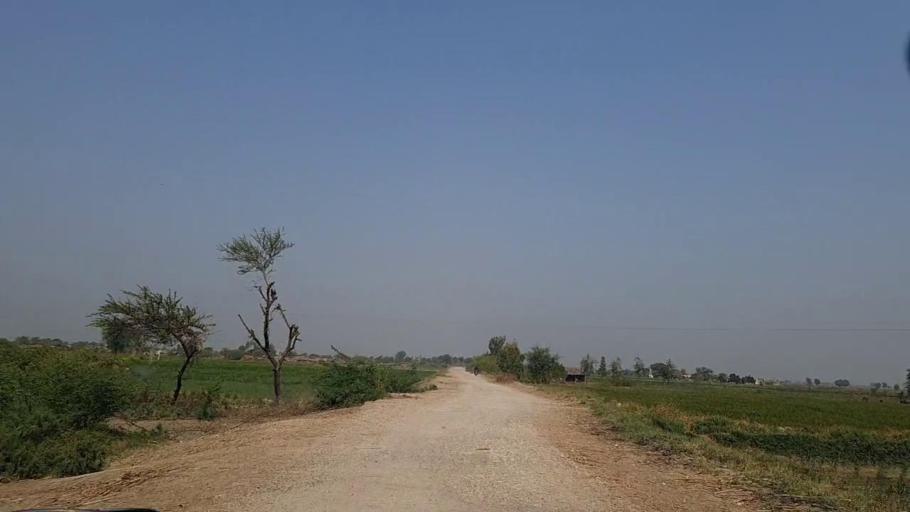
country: PK
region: Sindh
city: Mirpur Khas
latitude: 25.4937
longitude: 69.1916
